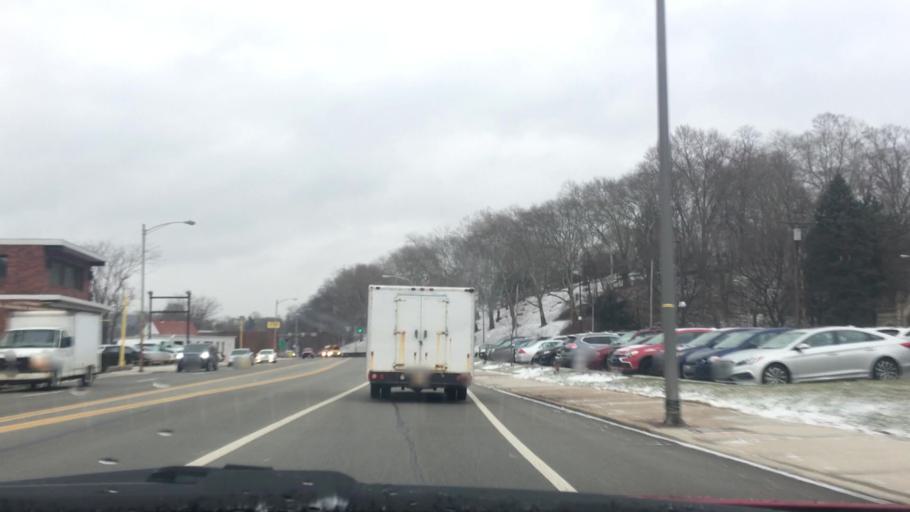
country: US
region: Pennsylvania
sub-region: Allegheny County
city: McKeesport
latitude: 40.3526
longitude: -79.8501
